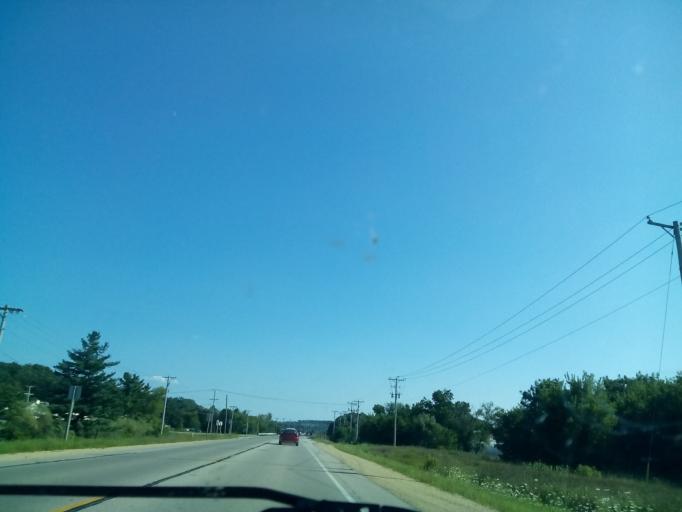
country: US
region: Wisconsin
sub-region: Green County
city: New Glarus
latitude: 42.8194
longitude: -89.6330
